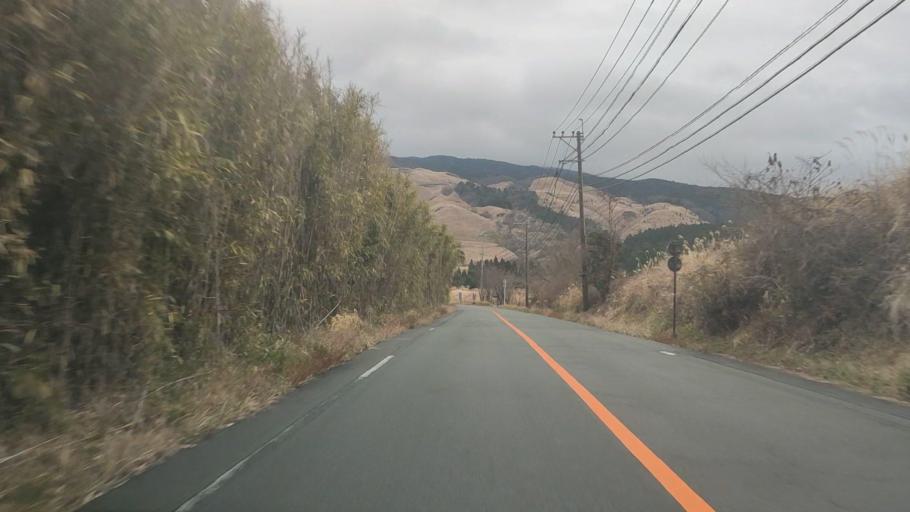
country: JP
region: Kumamoto
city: Aso
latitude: 32.8909
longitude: 131.0219
